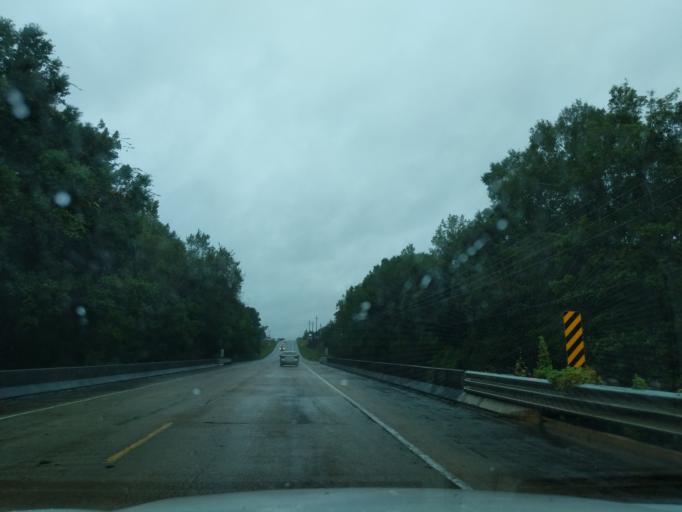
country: US
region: Louisiana
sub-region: Webster Parish
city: Minden
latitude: 32.6207
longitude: -93.2497
